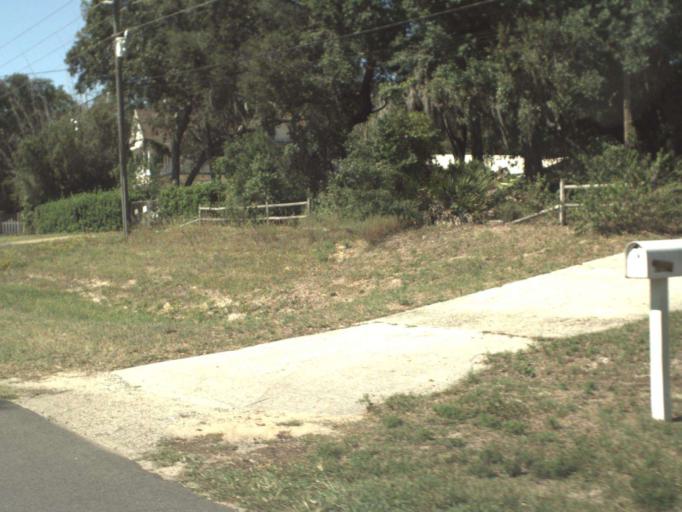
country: US
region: Florida
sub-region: Walton County
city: Miramar Beach
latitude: 30.4660
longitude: -86.3557
